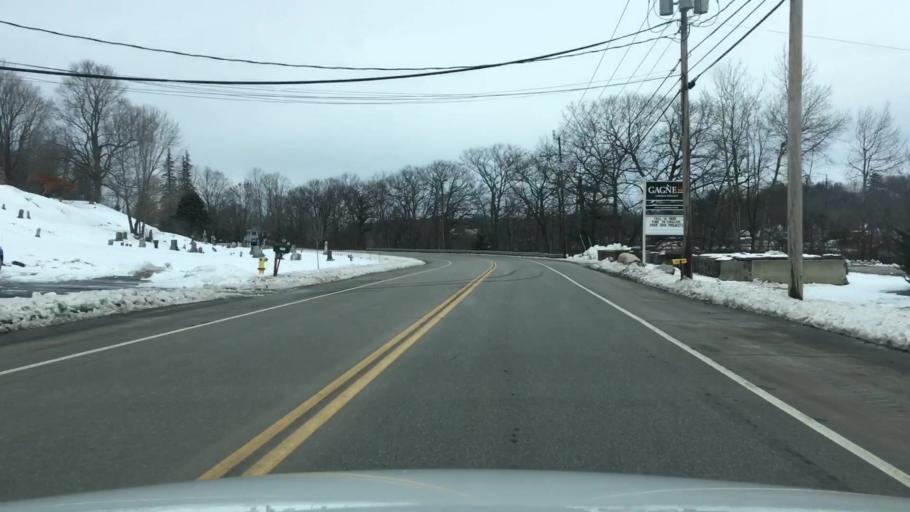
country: US
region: Maine
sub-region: Androscoggin County
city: Lewiston
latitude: 44.0794
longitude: -70.2108
